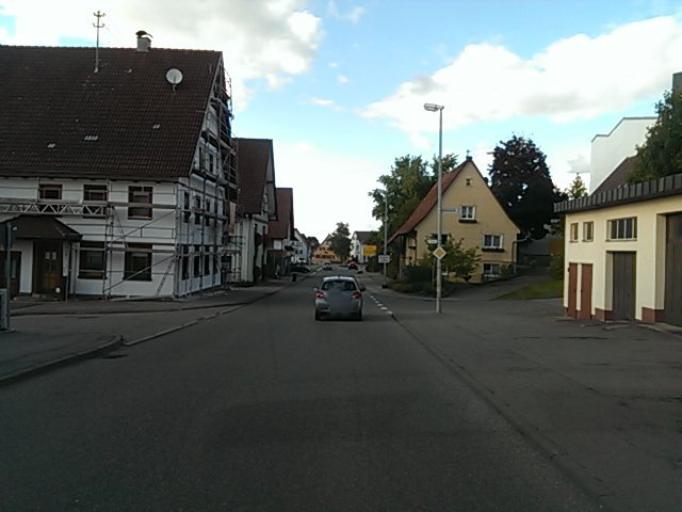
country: DE
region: Baden-Wuerttemberg
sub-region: Freiburg Region
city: Seedorf
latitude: 48.2675
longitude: 8.4859
